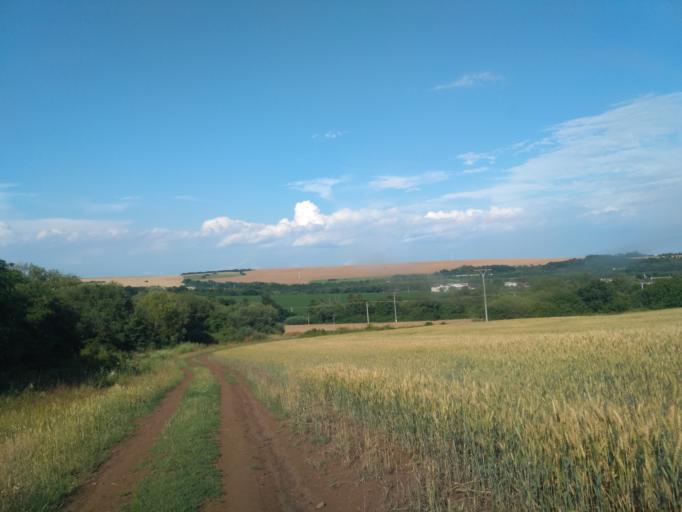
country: SK
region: Kosicky
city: Secovce
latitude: 48.6026
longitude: 21.5476
